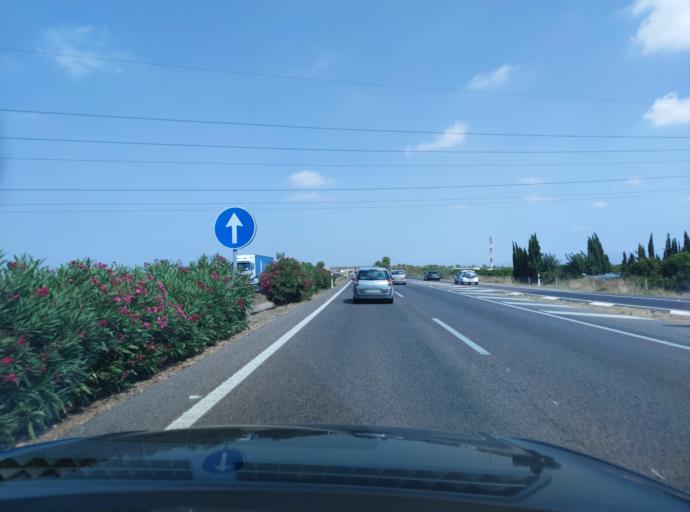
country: ES
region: Valencia
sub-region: Provincia de Castello
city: Alquerias del Nino Perdido
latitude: 39.9010
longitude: -0.1337
